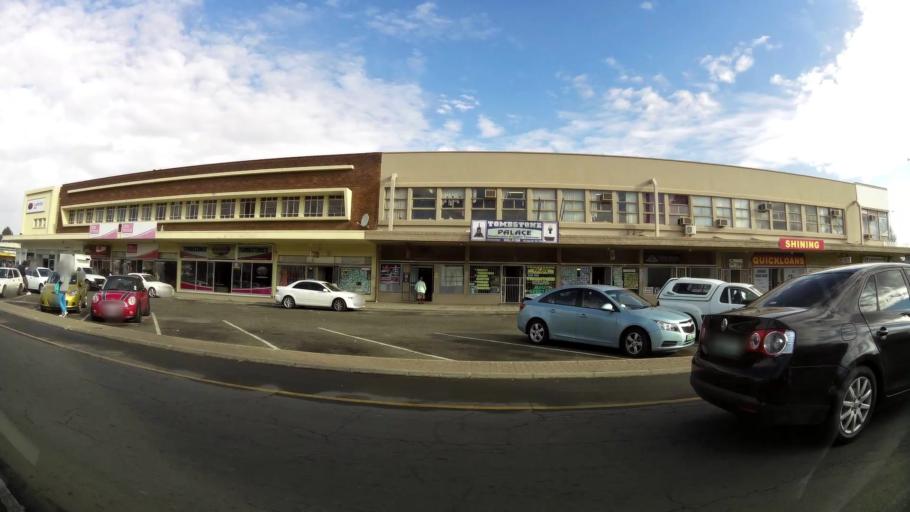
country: ZA
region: Orange Free State
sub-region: Lejweleputswa District Municipality
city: Welkom
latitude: -27.9813
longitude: 26.7397
